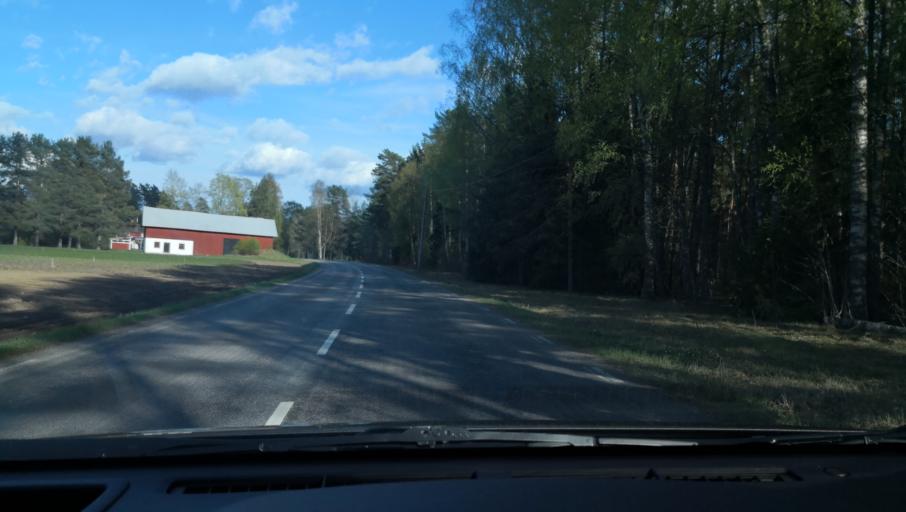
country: SE
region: OErebro
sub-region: Askersunds Kommun
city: Asbro
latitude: 58.9085
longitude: 15.0871
